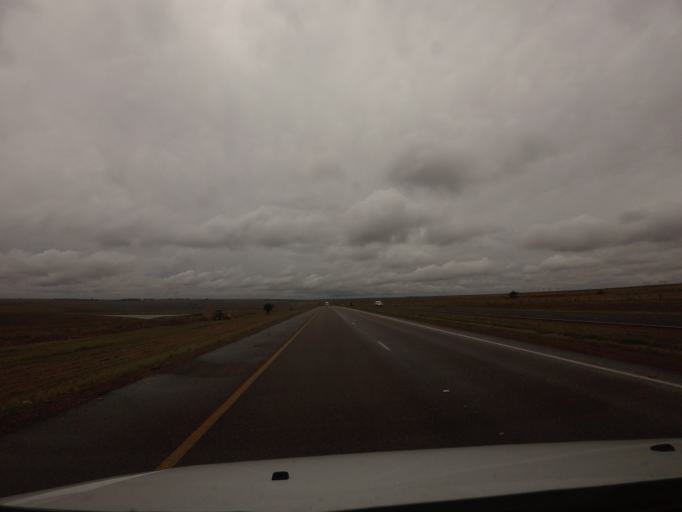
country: ZA
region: Mpumalanga
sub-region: Nkangala District Municipality
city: Middelburg
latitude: -25.8227
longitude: 29.5684
